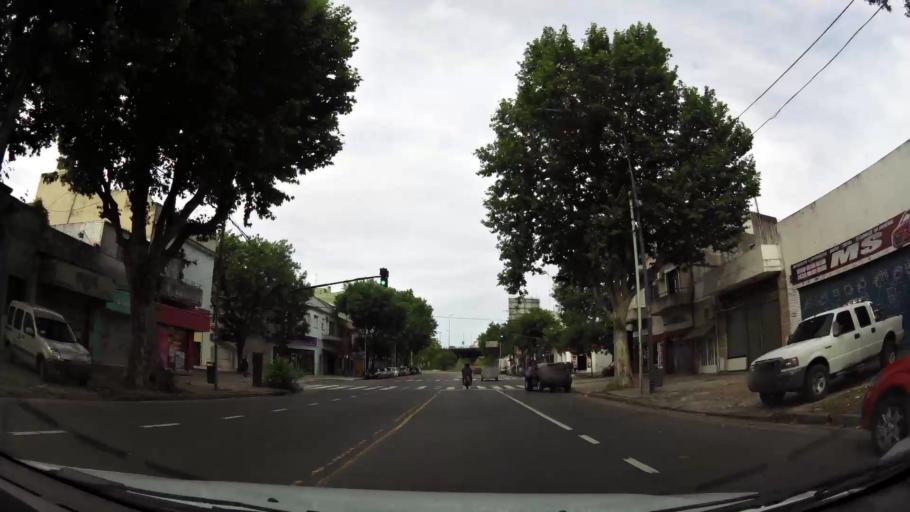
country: AR
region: Buenos Aires F.D.
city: Villa Lugano
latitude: -34.6445
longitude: -58.4642
